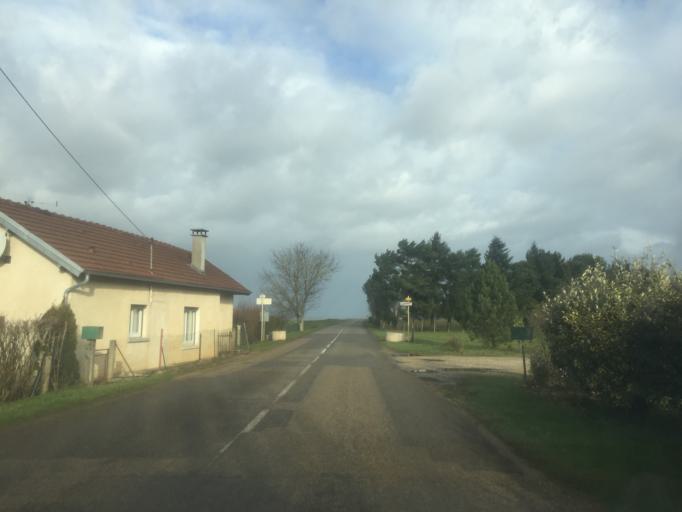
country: FR
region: Franche-Comte
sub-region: Departement du Jura
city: Orchamps
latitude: 47.2090
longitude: 5.6833
